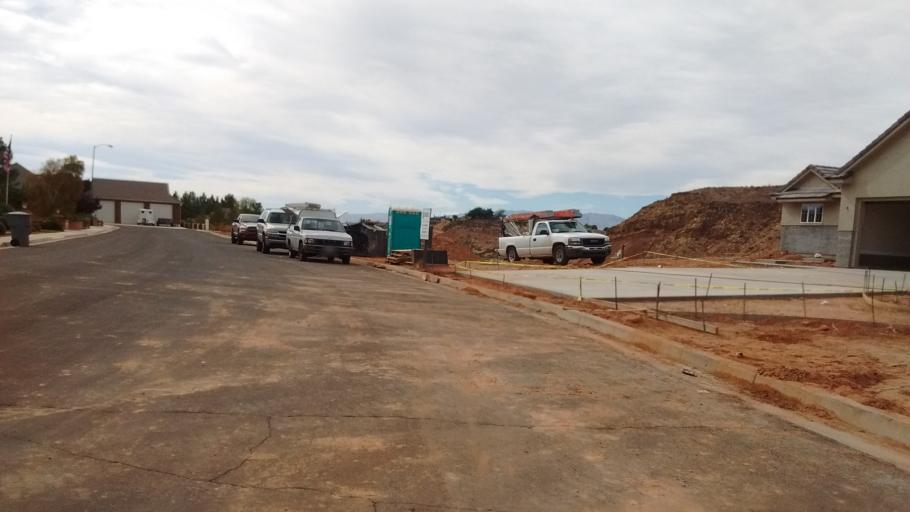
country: US
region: Utah
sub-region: Washington County
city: Washington
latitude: 37.1225
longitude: -113.4933
